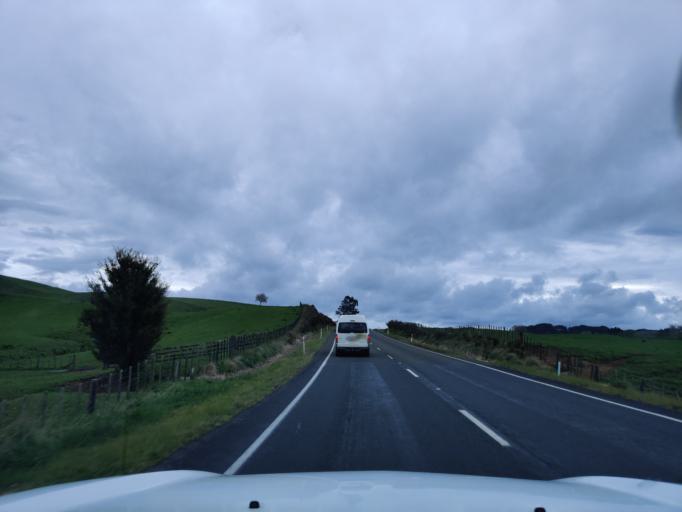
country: NZ
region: Waikato
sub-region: Otorohanga District
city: Otorohanga
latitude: -38.4559
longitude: 175.1669
